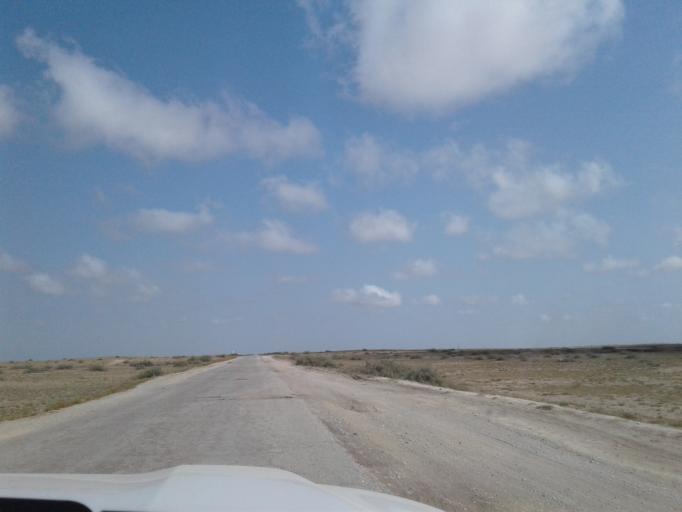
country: IR
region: Golestan
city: Gomishan
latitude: 37.6305
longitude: 53.9288
